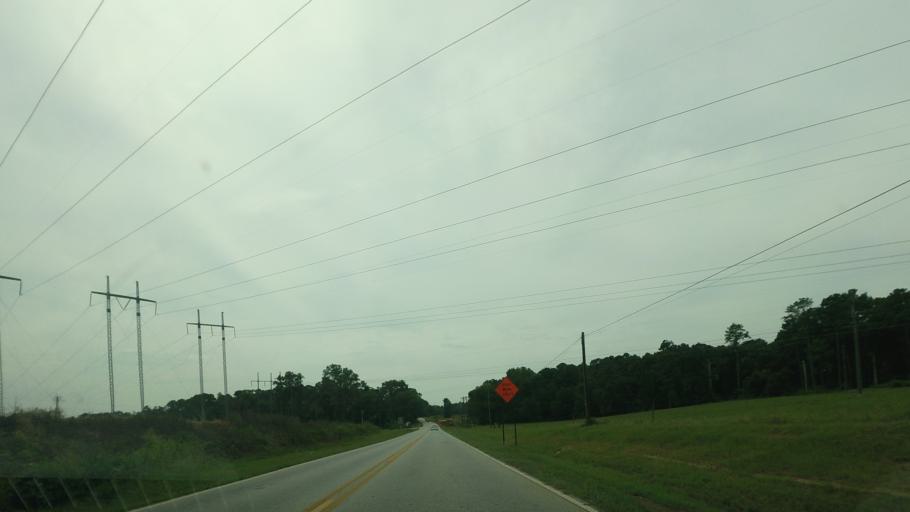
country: US
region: Georgia
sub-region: Houston County
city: Robins Air Force Base
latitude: 32.5581
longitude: -83.5862
